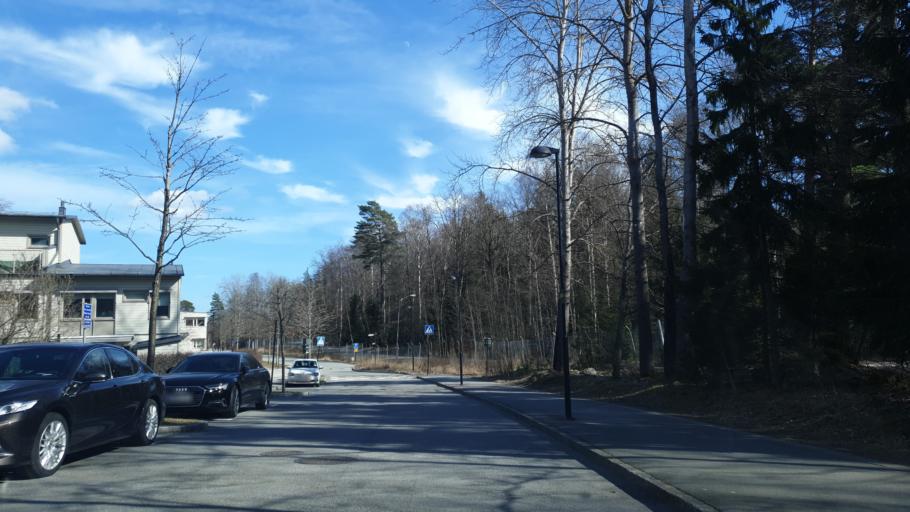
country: SE
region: Stockholm
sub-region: Solna Kommun
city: Rasunda
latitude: 59.3982
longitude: 17.9925
